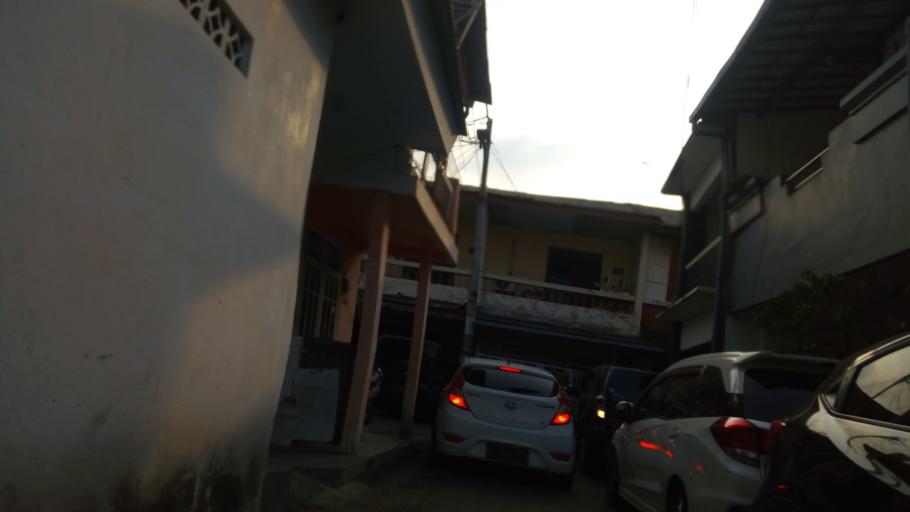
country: ID
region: Jakarta Raya
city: Jakarta
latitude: -6.2037
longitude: 106.8482
